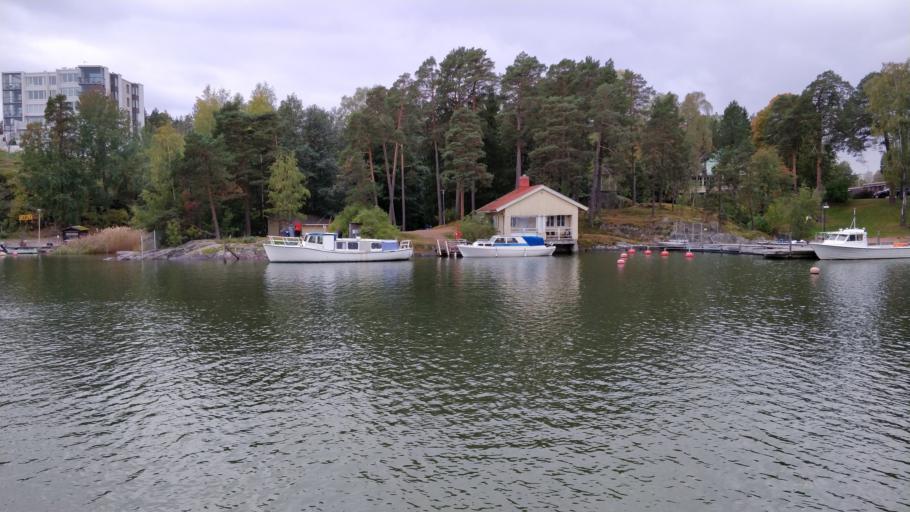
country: FI
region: Uusimaa
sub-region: Helsinki
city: Vantaa
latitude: 60.1841
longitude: 25.0644
